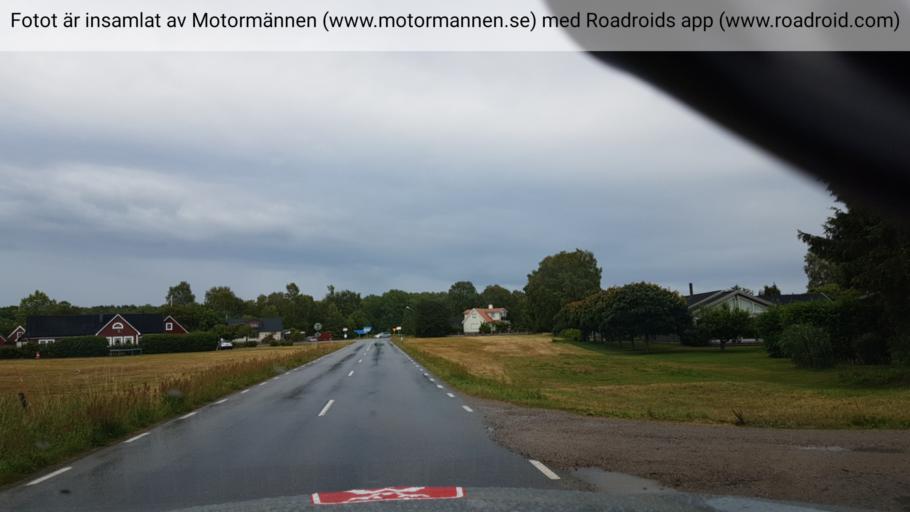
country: SE
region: Blekinge
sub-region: Solvesborgs Kommun
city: Soelvesborg
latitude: 56.0165
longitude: 14.7146
